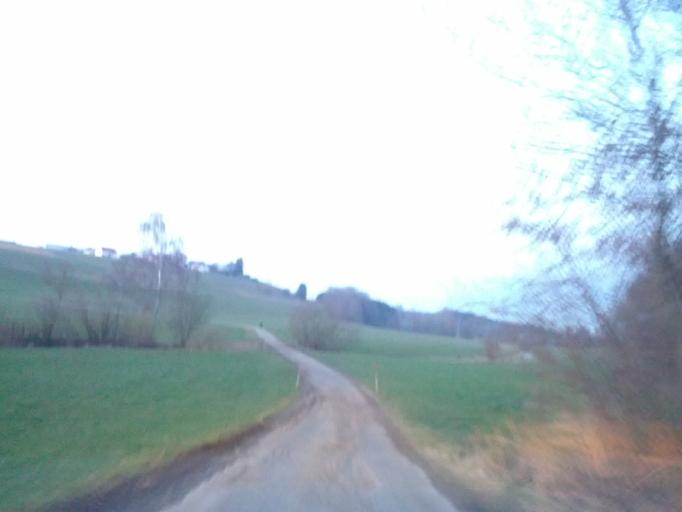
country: DE
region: Baden-Wuerttemberg
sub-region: Tuebingen Region
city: Steinhausen an der Rottum
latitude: 47.9789
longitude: 9.9877
